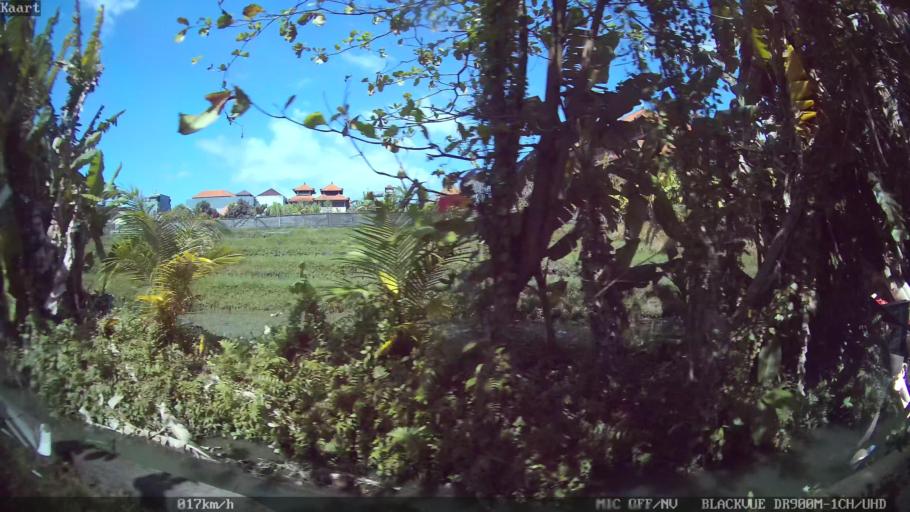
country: ID
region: Bali
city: Banjar Karangsuling
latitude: -8.6238
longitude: 115.1794
